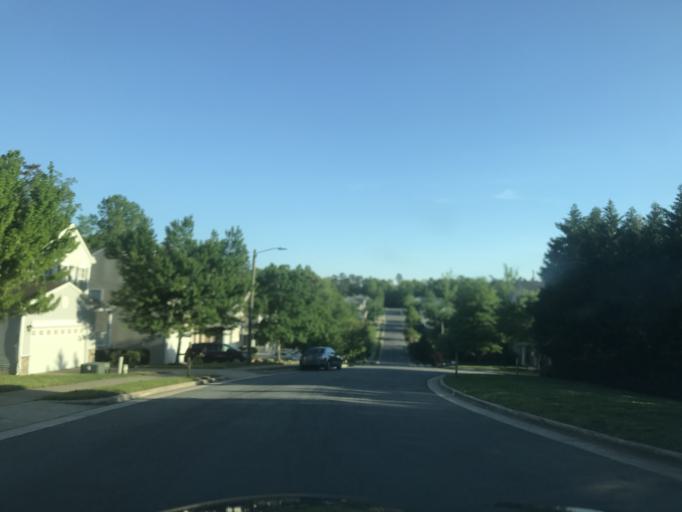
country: US
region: North Carolina
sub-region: Wake County
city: Knightdale
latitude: 35.8289
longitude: -78.5597
